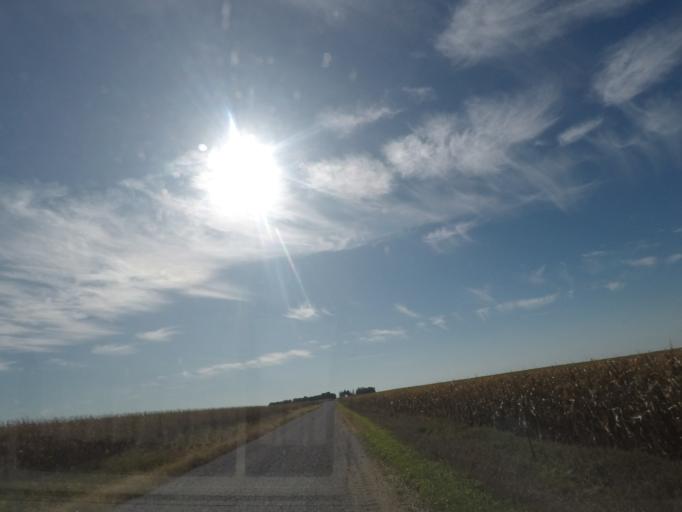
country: US
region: Iowa
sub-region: Story County
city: Nevada
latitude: 42.0598
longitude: -93.3288
